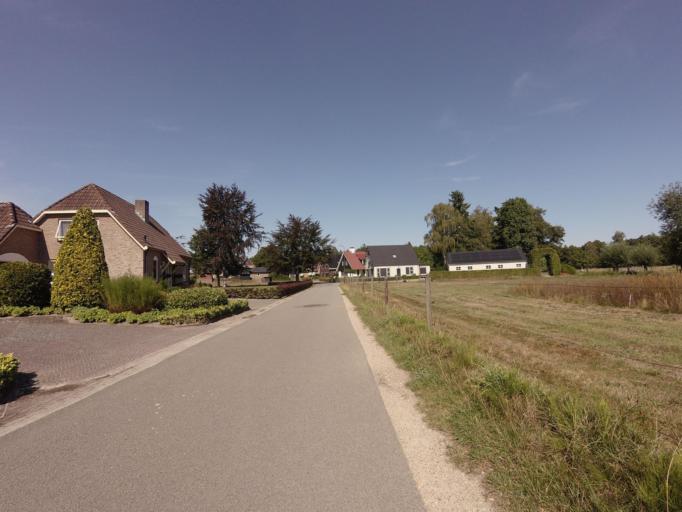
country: NL
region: Gelderland
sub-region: Gemeente Apeldoorn
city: Loenen
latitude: 52.1143
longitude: 6.0240
